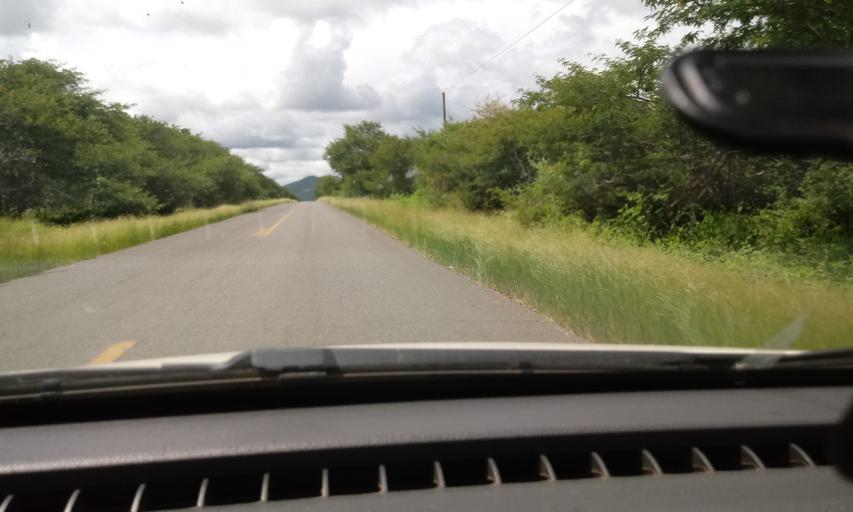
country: BR
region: Bahia
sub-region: Guanambi
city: Guanambi
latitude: -13.9297
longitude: -42.8479
